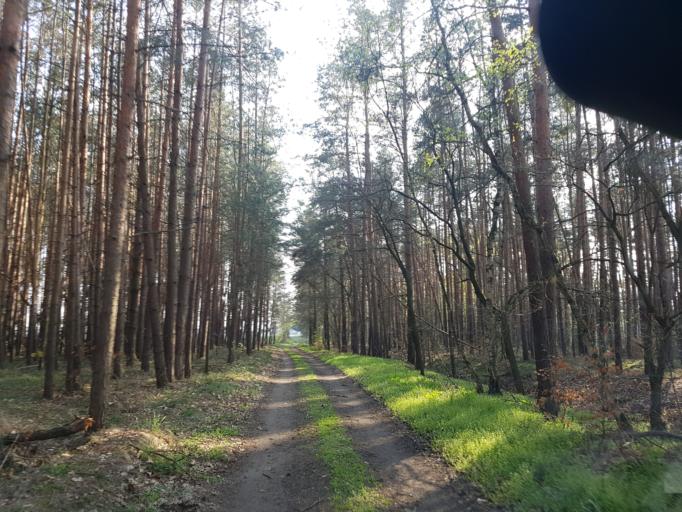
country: DE
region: Brandenburg
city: Schonborn
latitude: 51.6043
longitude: 13.5144
